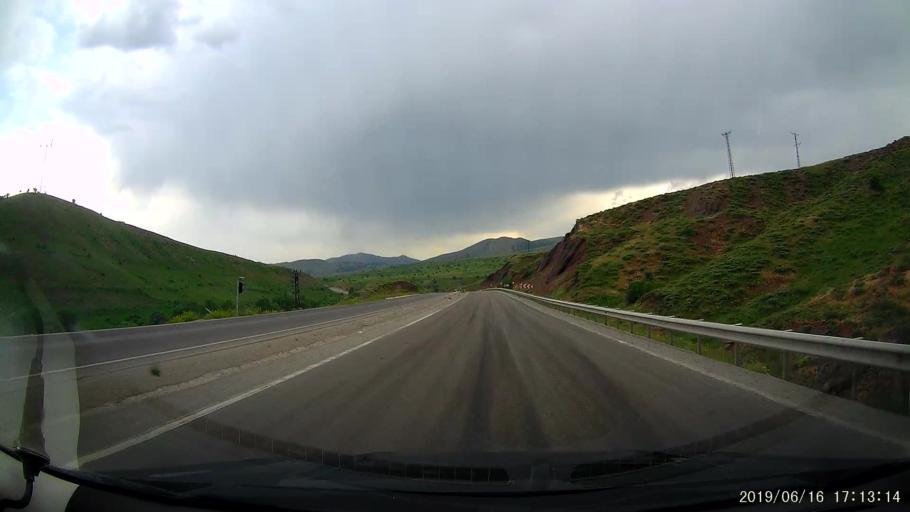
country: TR
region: Erzurum
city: Askale
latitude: 39.8598
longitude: 40.6027
